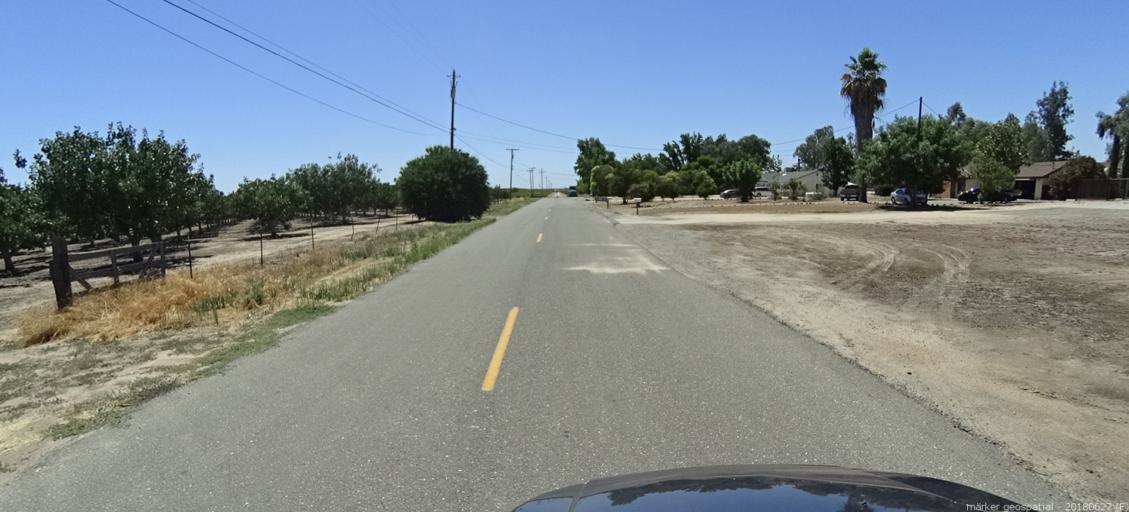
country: US
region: California
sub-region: Madera County
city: Bonadelle Ranchos-Madera Ranchos
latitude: 36.9593
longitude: -119.9167
